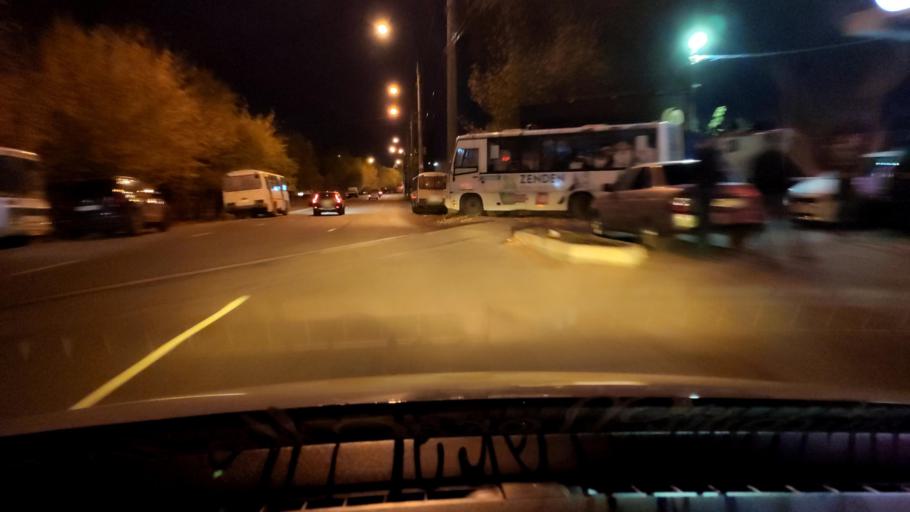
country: RU
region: Voronezj
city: Voronezh
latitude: 51.6773
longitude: 39.1683
